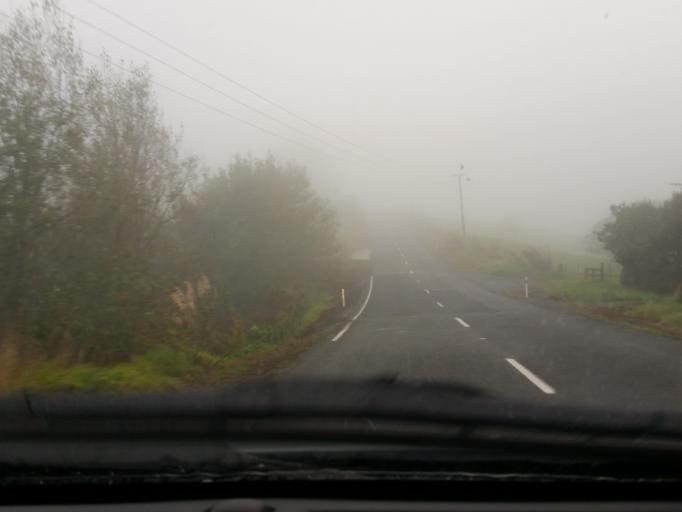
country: NZ
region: Northland
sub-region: Kaipara District
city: Dargaville
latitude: -35.9558
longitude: 173.9224
